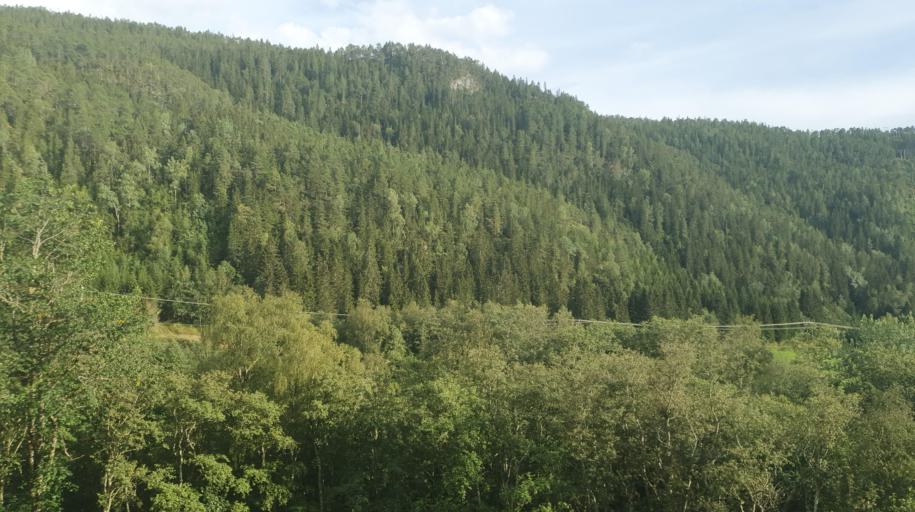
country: NO
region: Nord-Trondelag
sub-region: Stjordal
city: Stjordalshalsen
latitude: 63.5922
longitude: 11.0305
